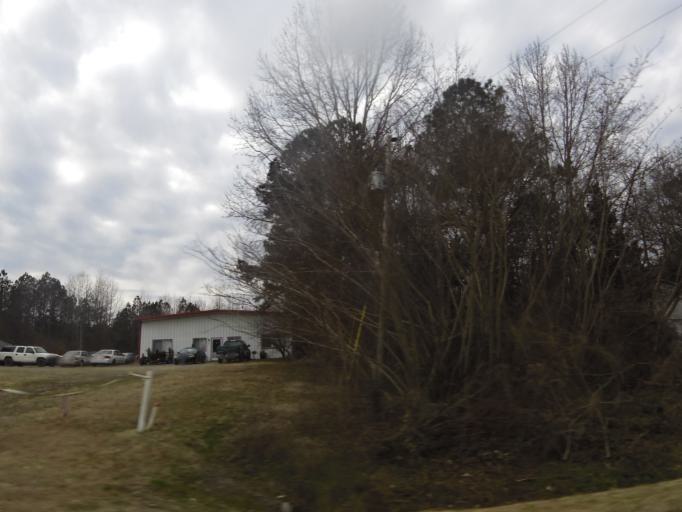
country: US
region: North Carolina
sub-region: Hertford County
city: Murfreesboro
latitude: 36.4316
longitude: -77.1404
